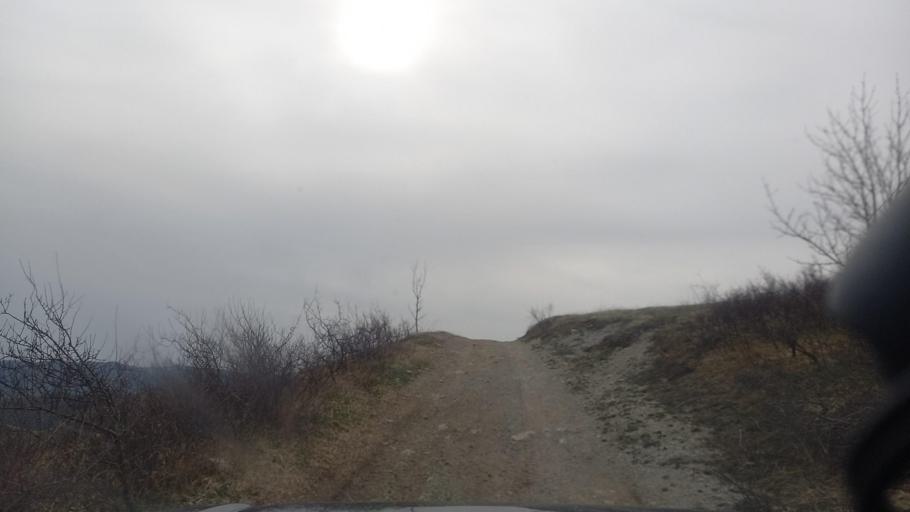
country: RU
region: Krasnodarskiy
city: Divnomorskoye
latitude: 44.6153
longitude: 38.2190
